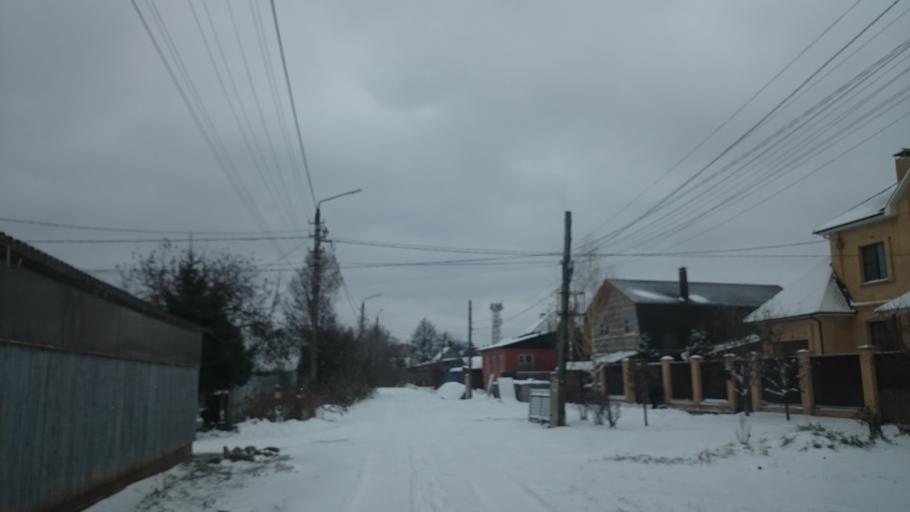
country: RU
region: Tula
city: Tula
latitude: 54.2013
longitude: 37.5649
